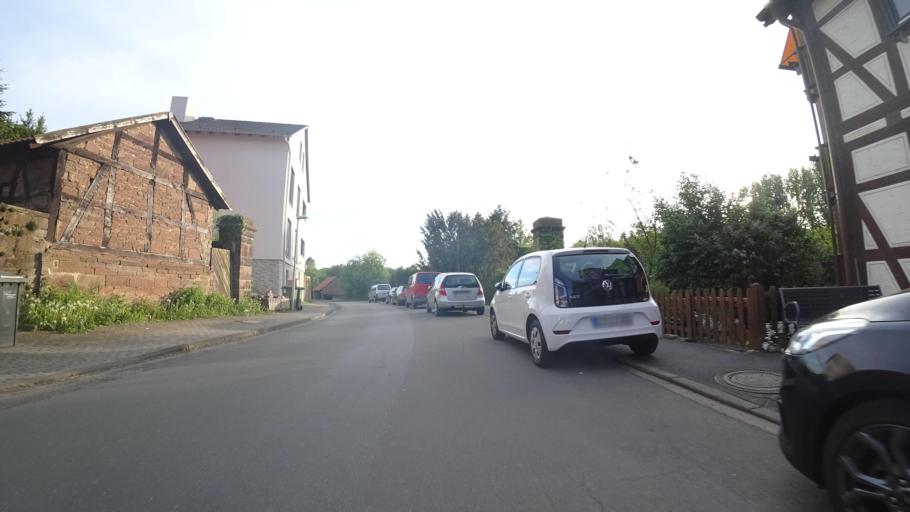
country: DE
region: Hesse
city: Grebenstein
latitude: 51.4445
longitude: 9.4136
